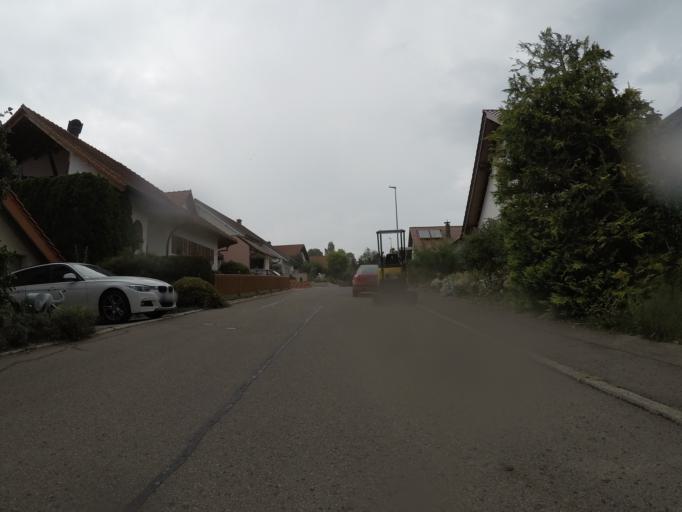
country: DE
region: Baden-Wuerttemberg
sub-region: Tuebingen Region
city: Eningen unter Achalm
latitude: 48.4873
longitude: 9.2468
